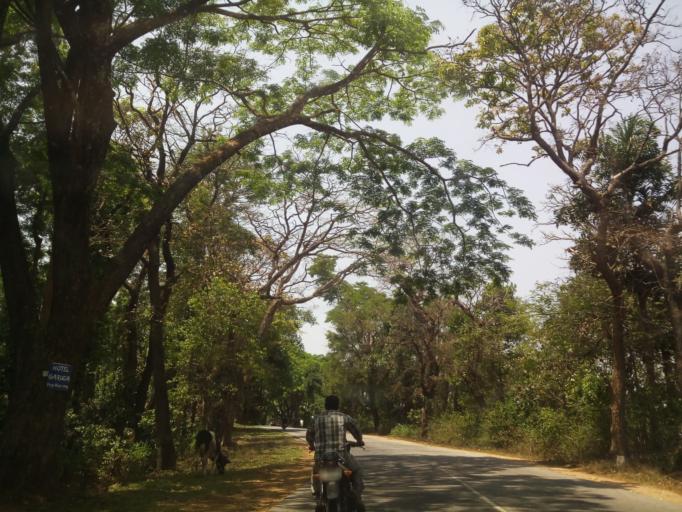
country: IN
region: Karnataka
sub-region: Hassan
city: Sakleshpur
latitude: 12.9544
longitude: 75.8621
